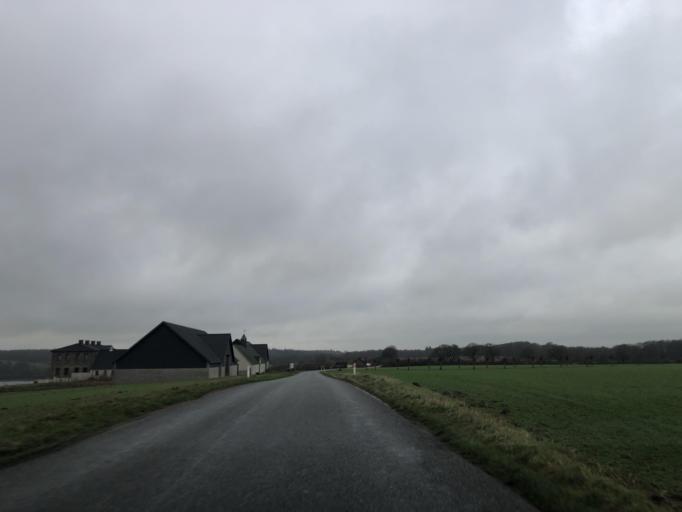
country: DK
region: Central Jutland
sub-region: Randers Kommune
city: Langa
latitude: 56.4788
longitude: 9.8676
